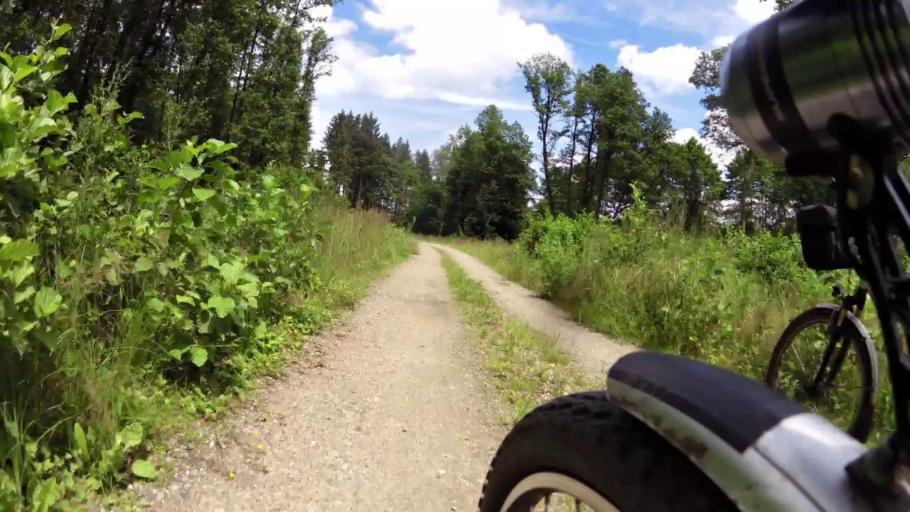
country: PL
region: West Pomeranian Voivodeship
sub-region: Powiat swidwinski
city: Rabino
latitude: 53.9018
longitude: 15.9957
